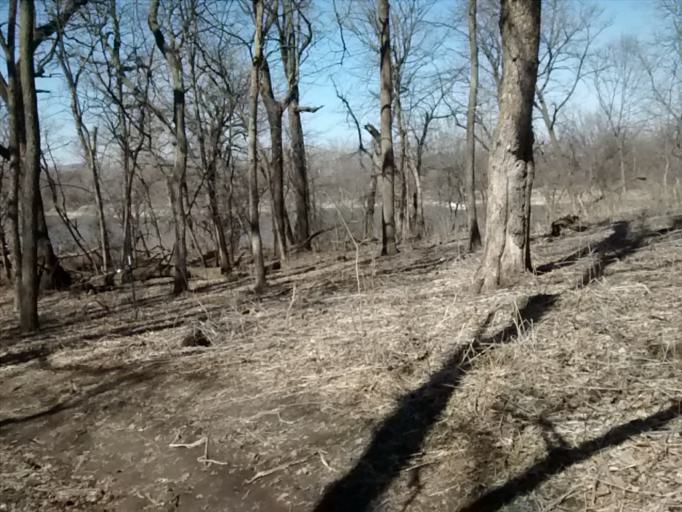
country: US
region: Nebraska
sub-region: Sarpy County
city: Bellevue
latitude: 41.1824
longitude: -95.9105
